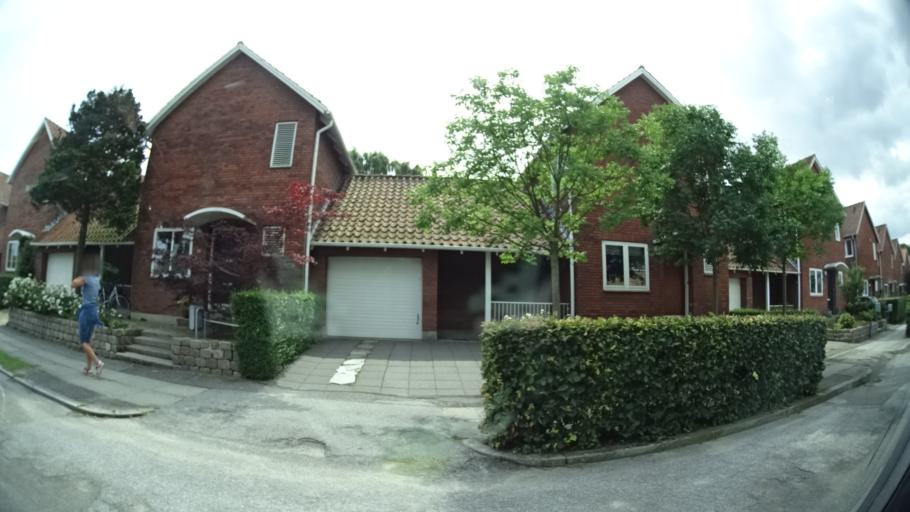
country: DK
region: Central Jutland
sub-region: Arhus Kommune
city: Arhus
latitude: 56.1370
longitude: 10.1878
